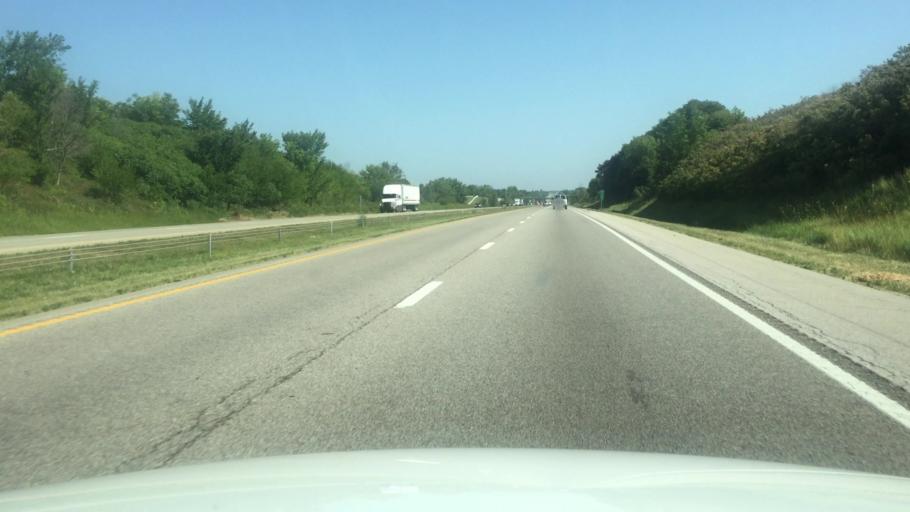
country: US
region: Missouri
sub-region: Platte County
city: Platte City
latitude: 39.5479
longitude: -94.7877
